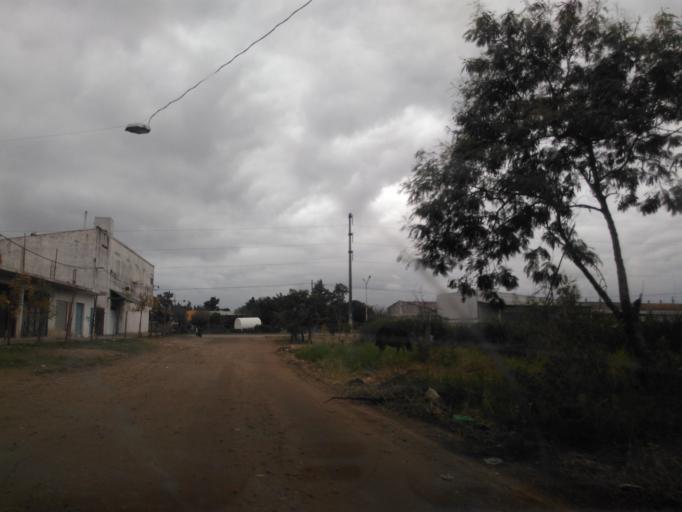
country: AR
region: Chaco
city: Fontana
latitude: -27.4286
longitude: -59.0133
